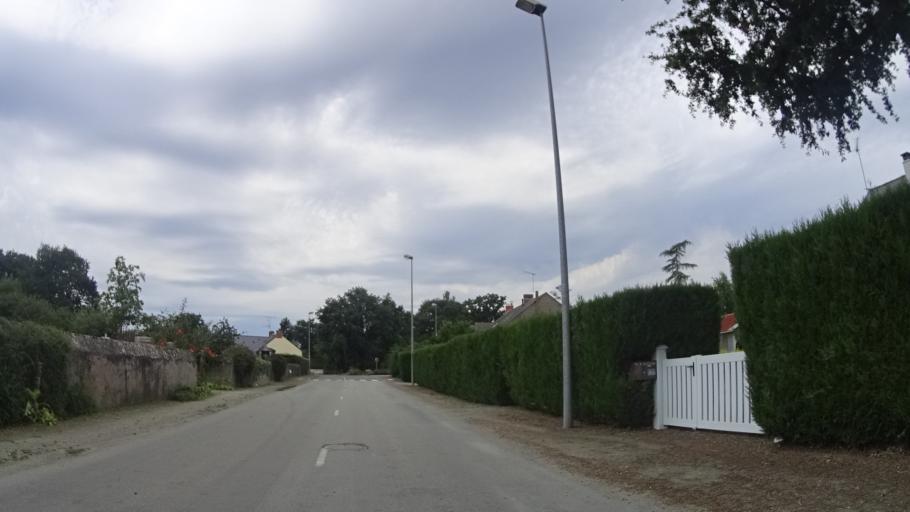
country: FR
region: Pays de la Loire
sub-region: Departement de la Loire-Atlantique
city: Heric
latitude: 47.4678
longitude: -1.6672
